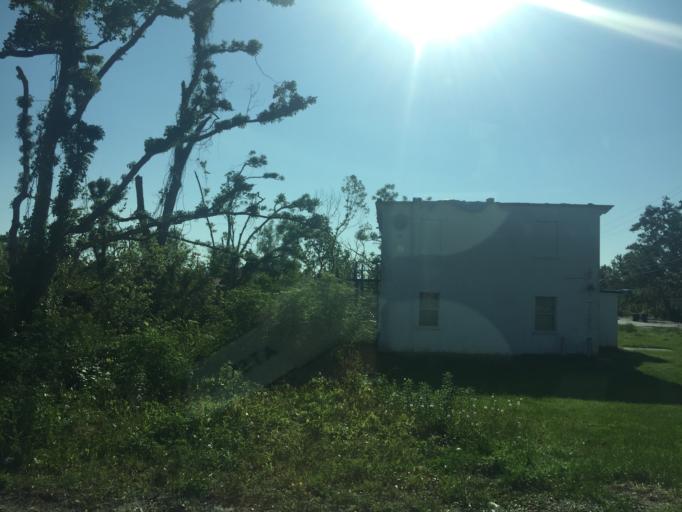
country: US
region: Florida
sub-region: Bay County
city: Cedar Grove
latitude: 30.1600
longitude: -85.6335
